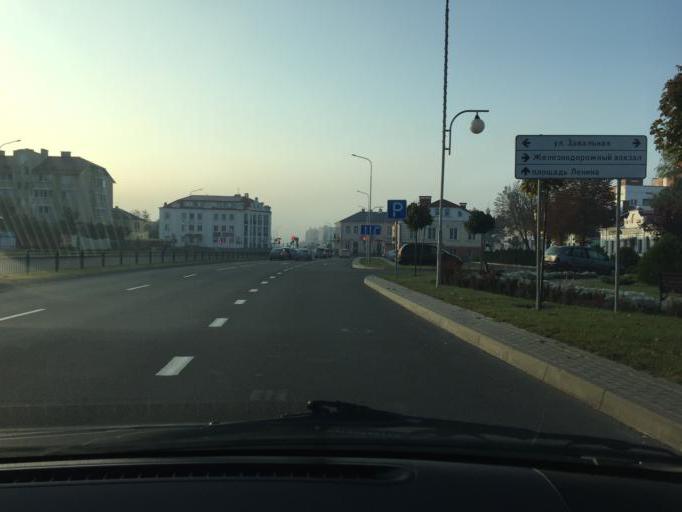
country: BY
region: Brest
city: Pinsk
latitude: 52.1166
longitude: 26.1024
